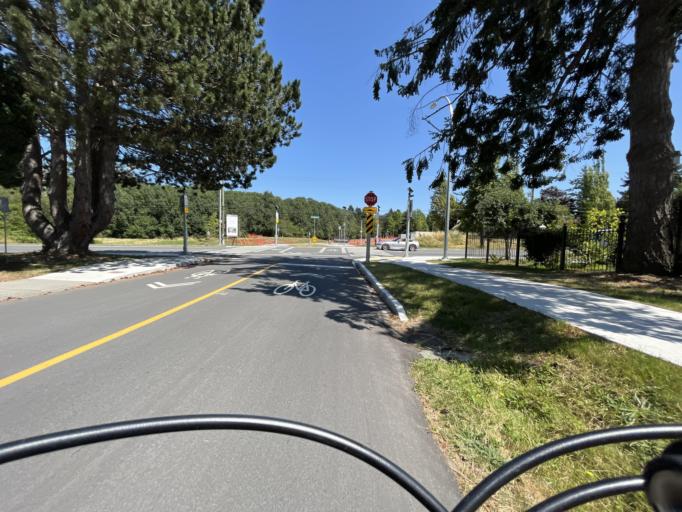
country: CA
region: British Columbia
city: Oak Bay
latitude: 48.4635
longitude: -123.3211
